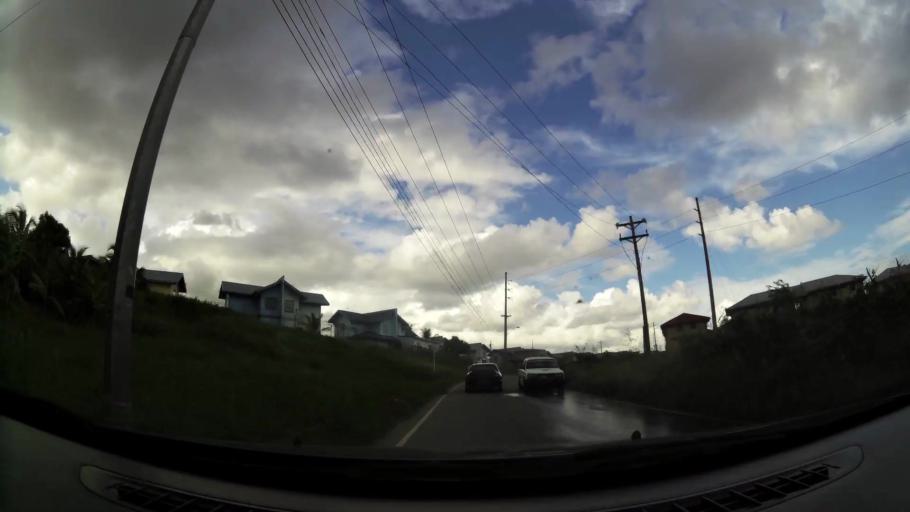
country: TT
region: City of San Fernando
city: Mon Repos
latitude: 10.2641
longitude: -61.4457
